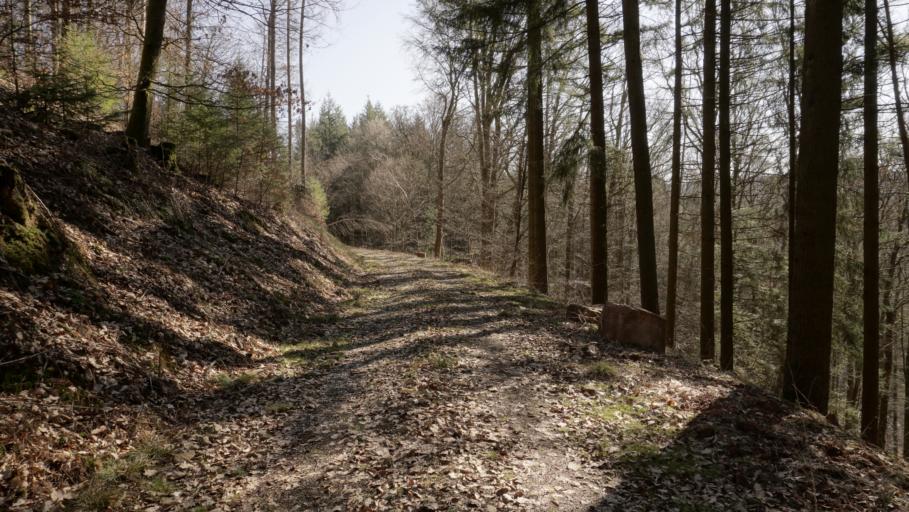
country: DE
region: Baden-Wuerttemberg
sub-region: Karlsruhe Region
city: Neckargerach
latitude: 49.4201
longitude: 9.1030
